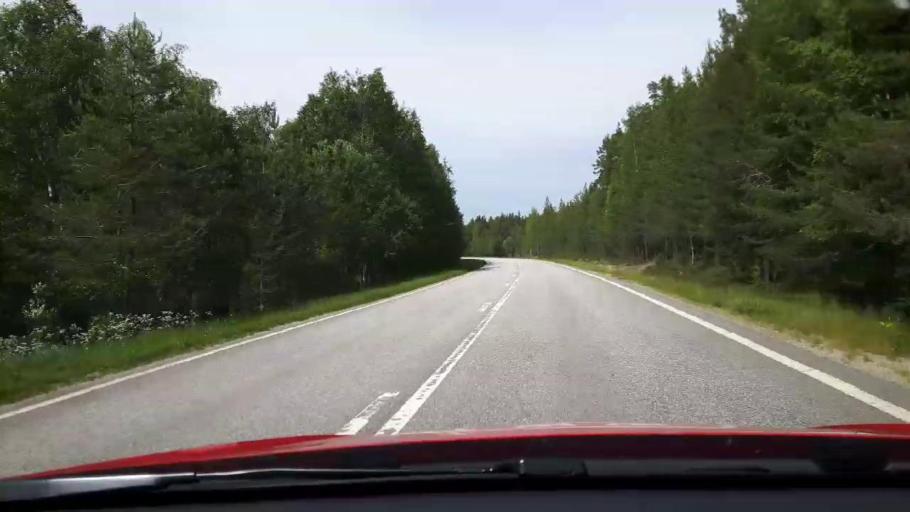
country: SE
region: Jaemtland
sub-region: Harjedalens Kommun
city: Sveg
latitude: 62.1325
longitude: 14.0549
